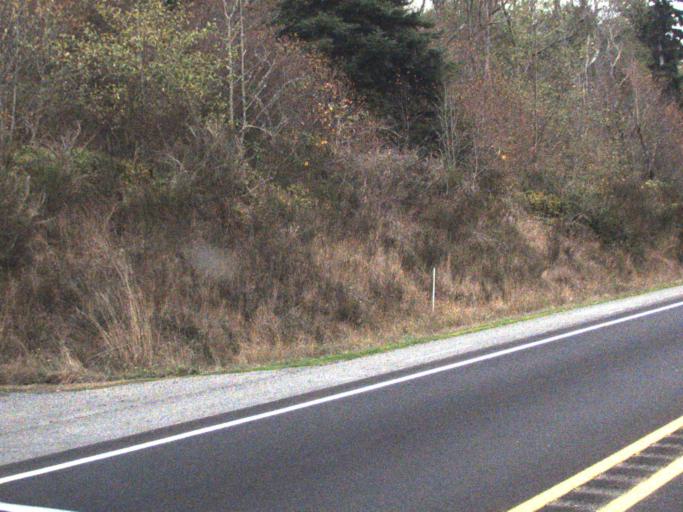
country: US
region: Washington
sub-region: Island County
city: Camano
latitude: 48.1421
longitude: -122.5929
